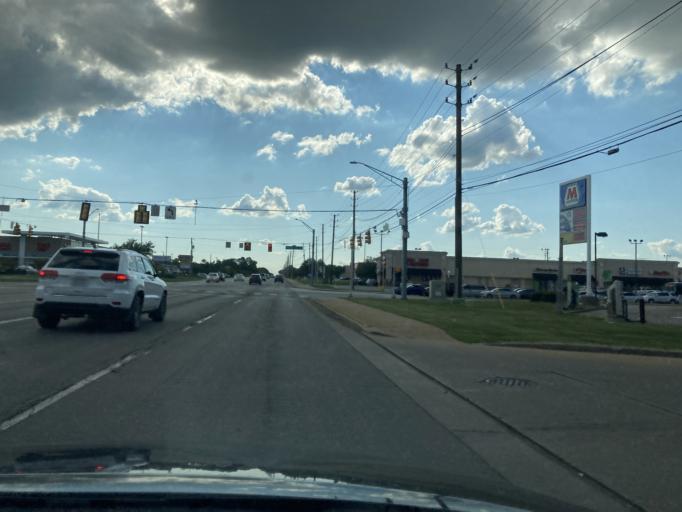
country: US
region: Indiana
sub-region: Marion County
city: Speedway
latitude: 39.8534
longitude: -86.2393
